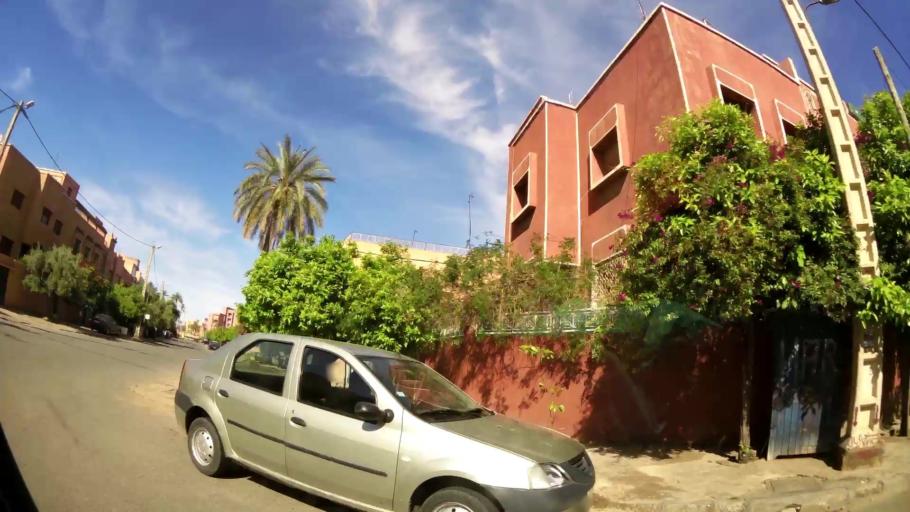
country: MA
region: Marrakech-Tensift-Al Haouz
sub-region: Marrakech
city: Marrakesh
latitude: 31.6449
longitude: -8.0077
